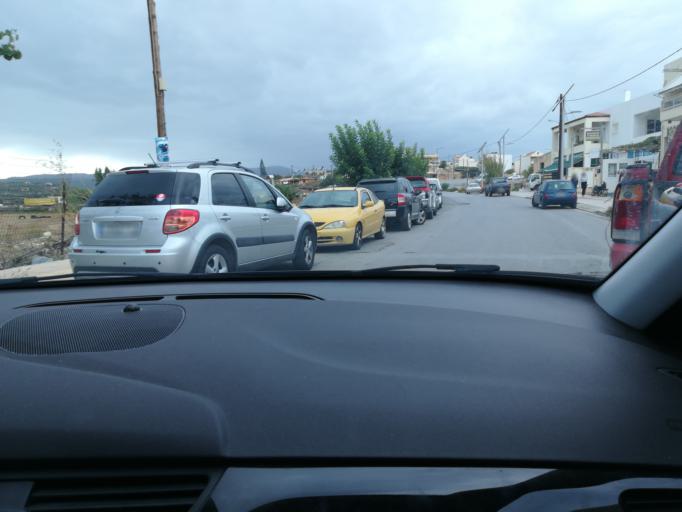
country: GR
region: Crete
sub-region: Nomos Lasithiou
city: Siteia
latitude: 35.2043
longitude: 26.1031
